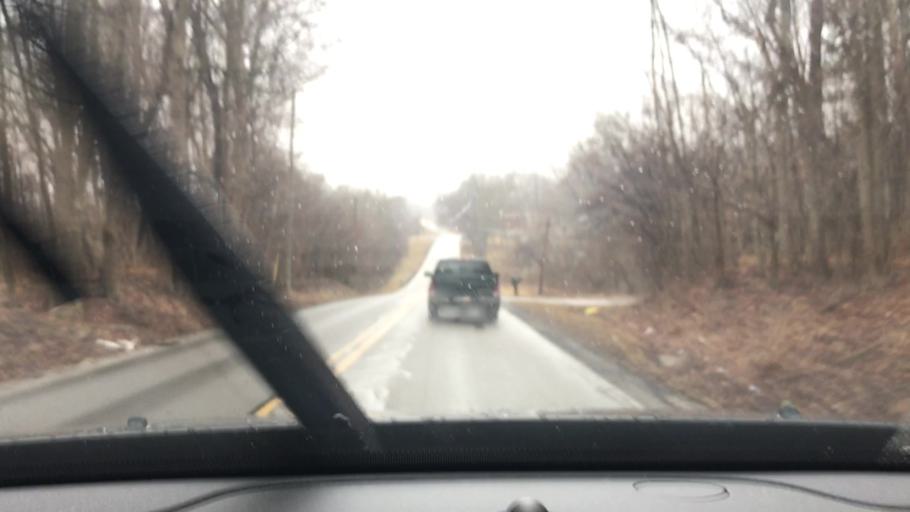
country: US
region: Indiana
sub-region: Morgan County
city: Mooresville
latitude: 39.5920
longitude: -86.3382
